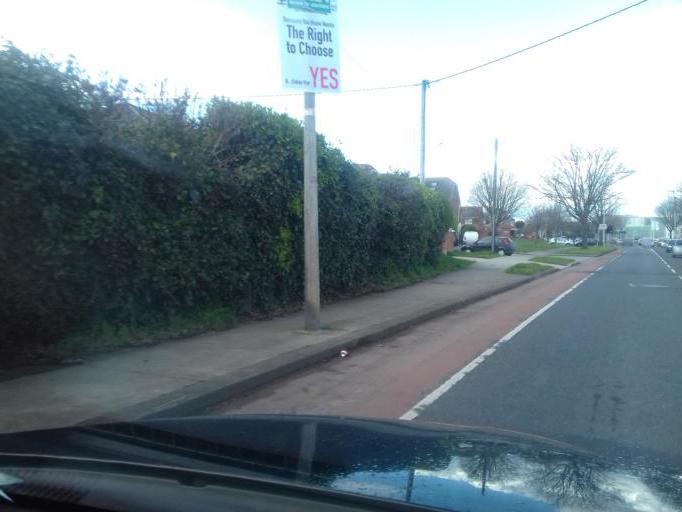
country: IE
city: Bayside
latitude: 53.3884
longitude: -6.1512
